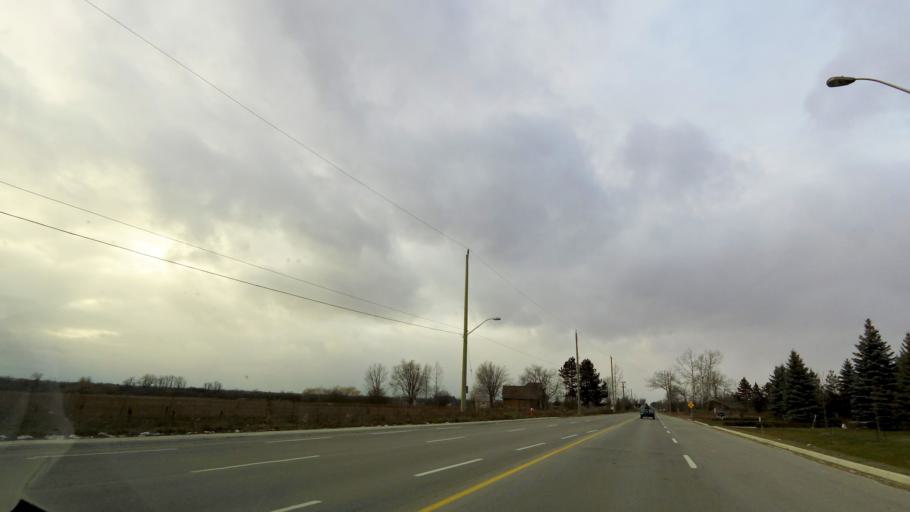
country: CA
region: Ontario
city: Brampton
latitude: 43.8019
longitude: -79.6797
